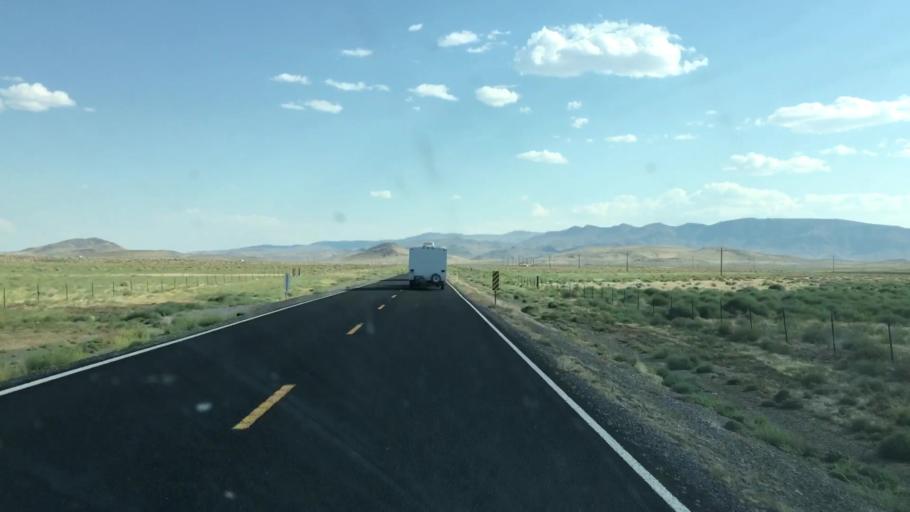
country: US
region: Nevada
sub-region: Lyon County
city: Fernley
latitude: 39.6629
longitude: -119.3325
